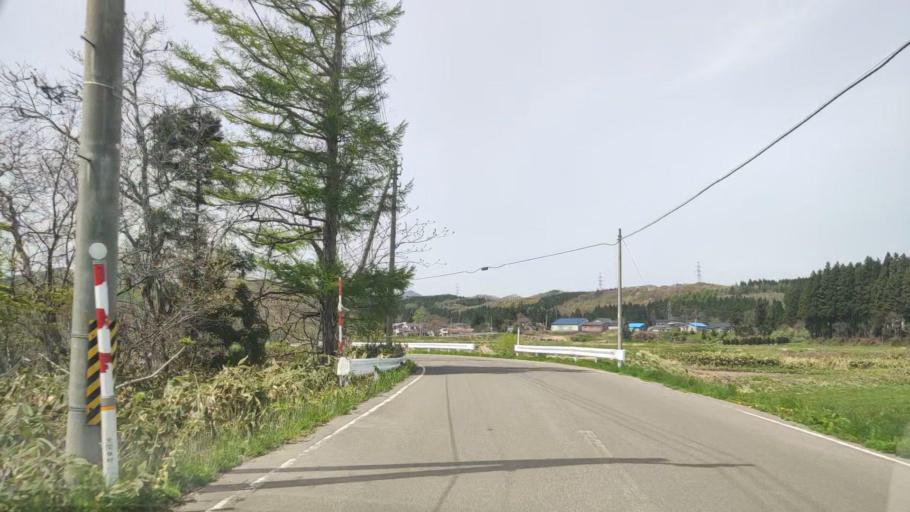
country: JP
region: Aomori
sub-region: Misawa Shi
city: Inuotose
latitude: 40.7856
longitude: 141.1127
